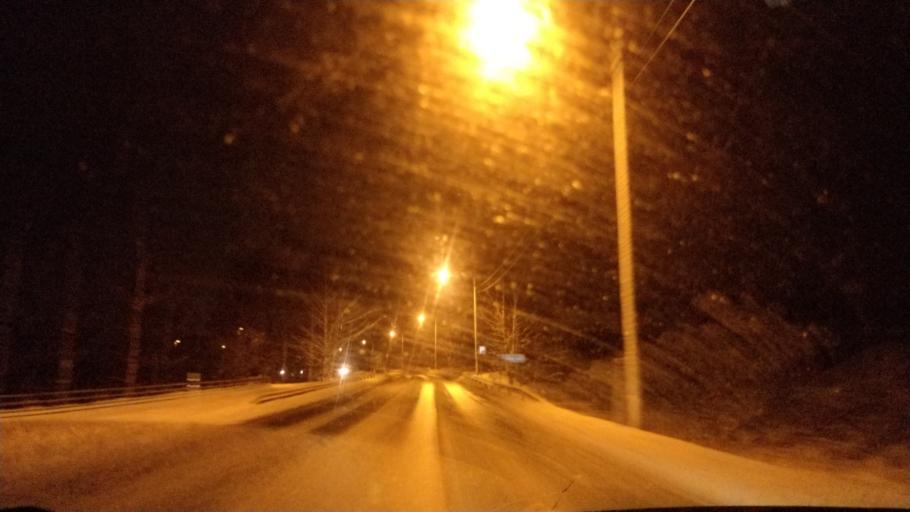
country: FI
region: Lapland
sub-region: Rovaniemi
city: Rovaniemi
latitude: 66.3931
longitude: 25.3809
